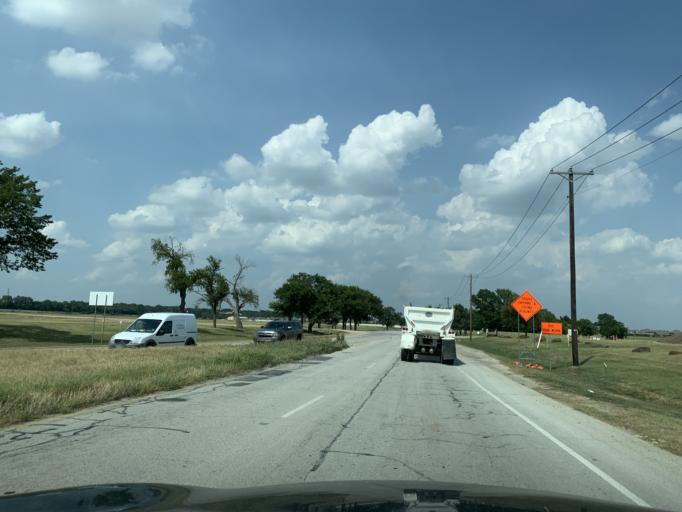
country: US
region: Texas
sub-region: Tarrant County
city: Richland Hills
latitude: 32.7982
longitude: -97.2092
